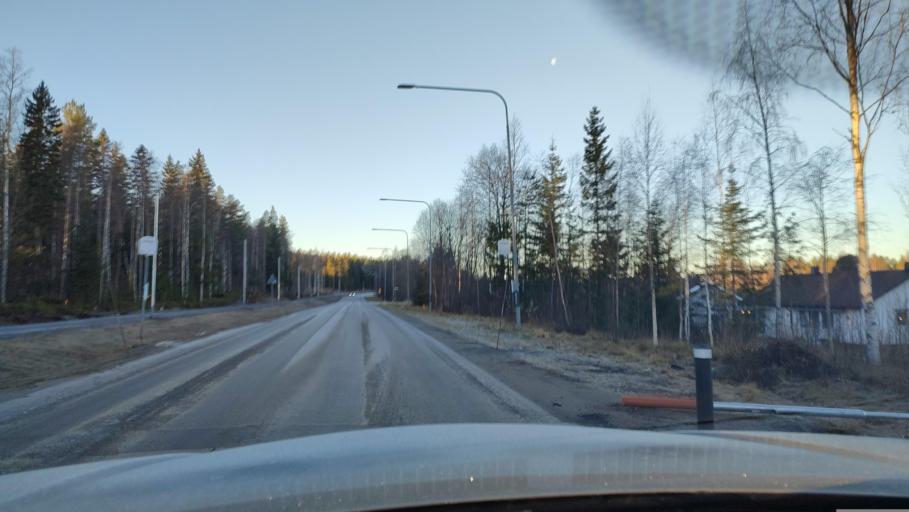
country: SE
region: Vaesterbotten
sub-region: Skelleftea Kommun
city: Skelleftea
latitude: 64.7398
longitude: 20.9333
